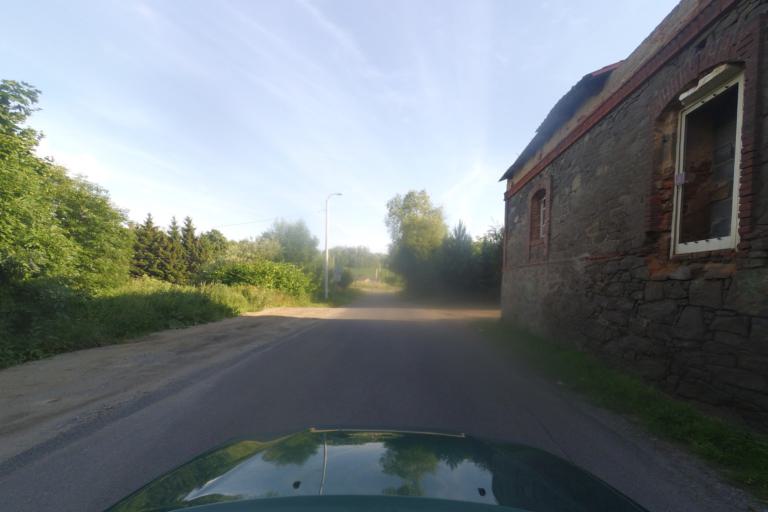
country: PL
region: Lower Silesian Voivodeship
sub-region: Powiat dzierzoniowski
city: Niemcza
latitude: 50.7164
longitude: 16.8309
